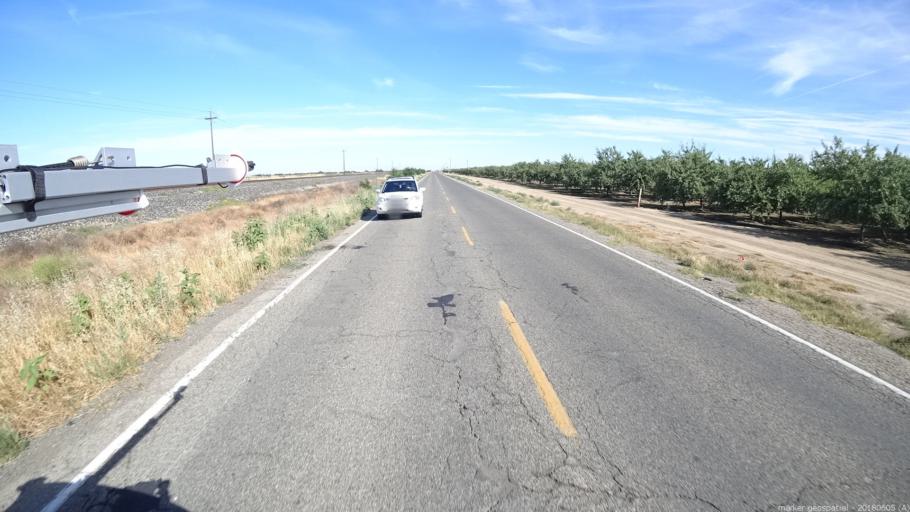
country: US
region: California
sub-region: Madera County
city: Chowchilla
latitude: 37.1295
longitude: -120.2626
